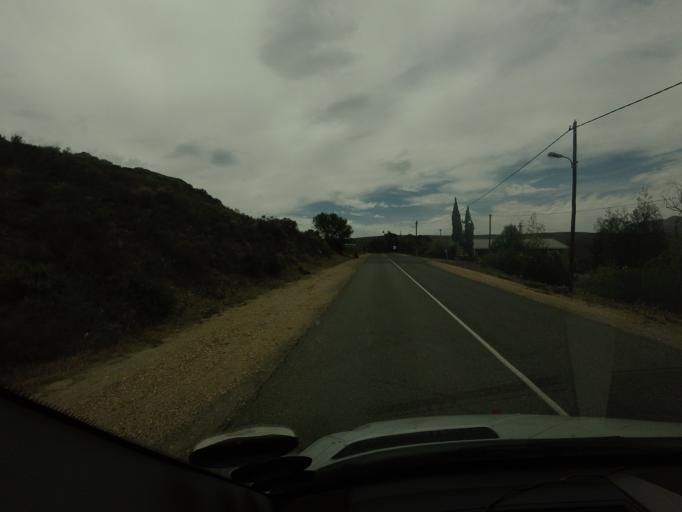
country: ZA
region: Western Cape
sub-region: Overberg District Municipality
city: Swellendam
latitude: -33.9010
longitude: 20.7218
